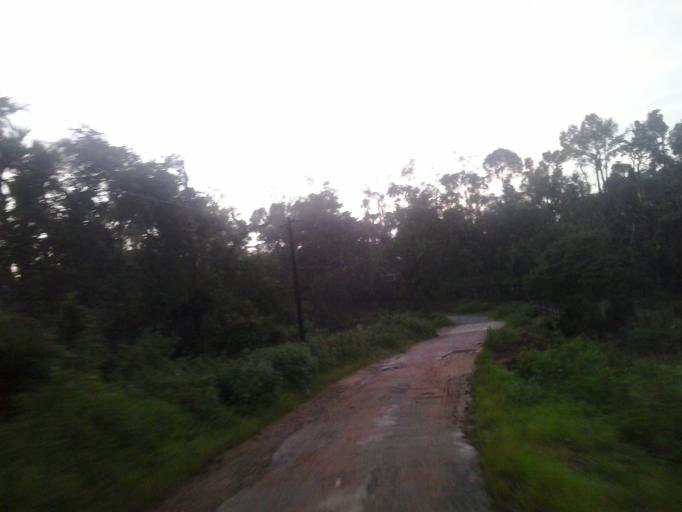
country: IN
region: Karnataka
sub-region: Chikmagalur
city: Mudigere
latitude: 13.0127
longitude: 75.6677
